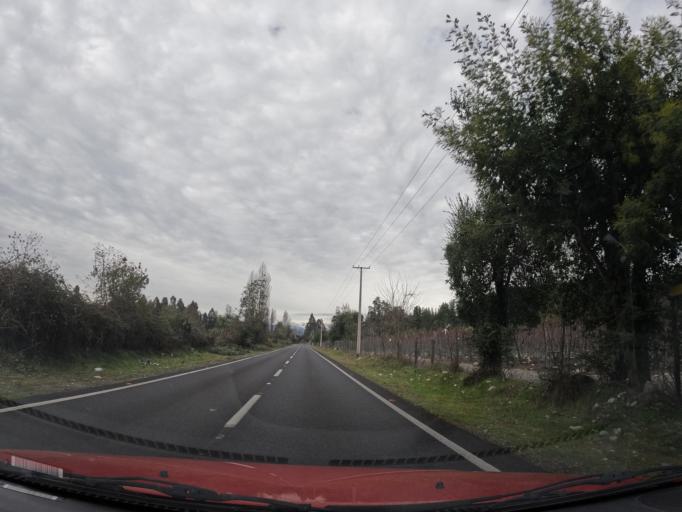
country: CL
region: Maule
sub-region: Provincia de Linares
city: Linares
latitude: -35.9117
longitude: -71.4859
